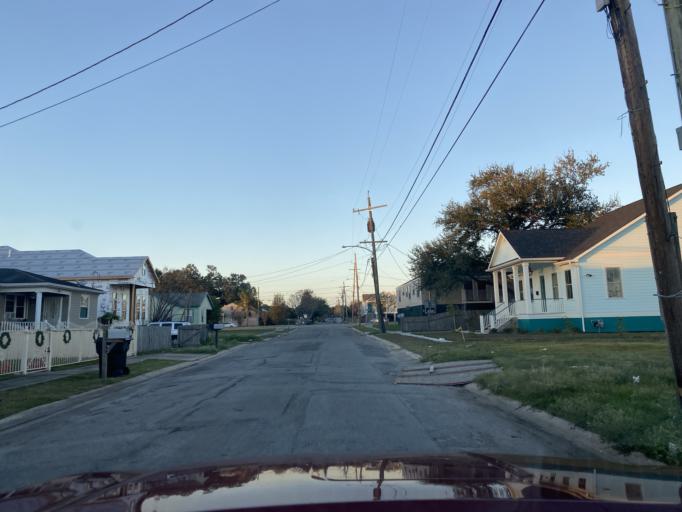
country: US
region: Louisiana
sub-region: Orleans Parish
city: New Orleans
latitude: 30.0215
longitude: -90.0552
